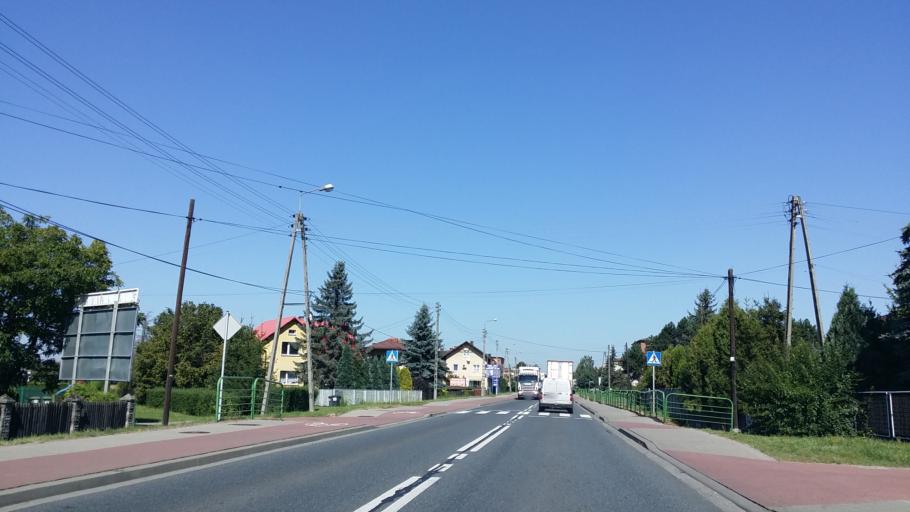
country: PL
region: Silesian Voivodeship
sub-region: Powiat bierunsko-ledzinski
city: Imielin
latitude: 50.1500
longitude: 19.1827
